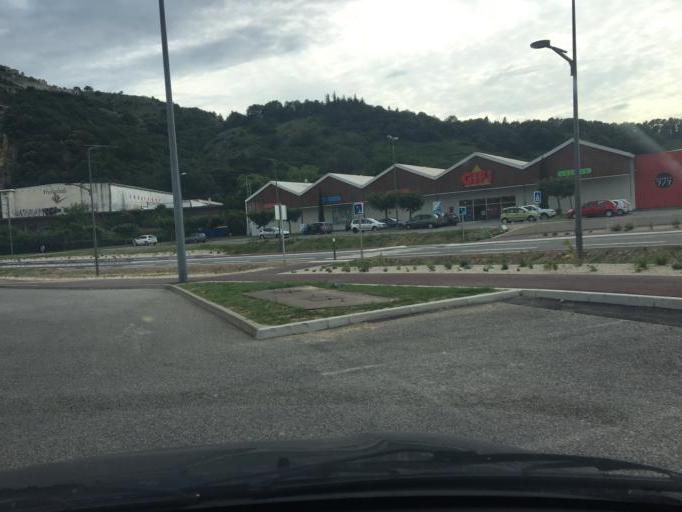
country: FR
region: Rhone-Alpes
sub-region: Departement de l'Ardeche
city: Saint-Peray
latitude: 44.9443
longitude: 4.8564
